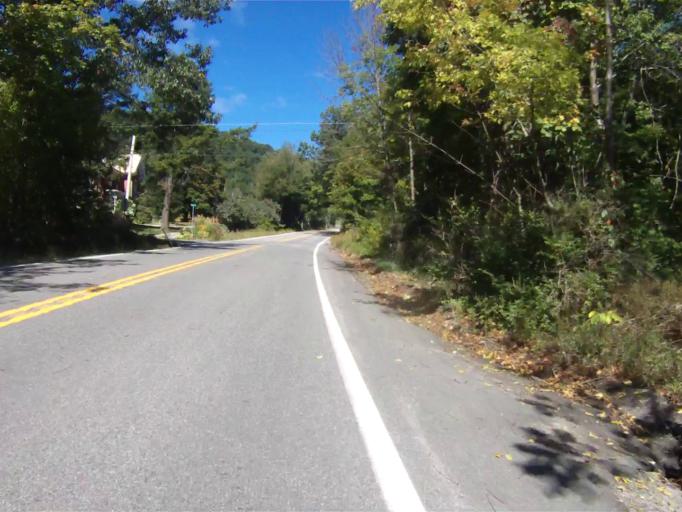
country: US
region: Pennsylvania
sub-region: Centre County
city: Park Forest Village
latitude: 40.9282
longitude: -77.9261
